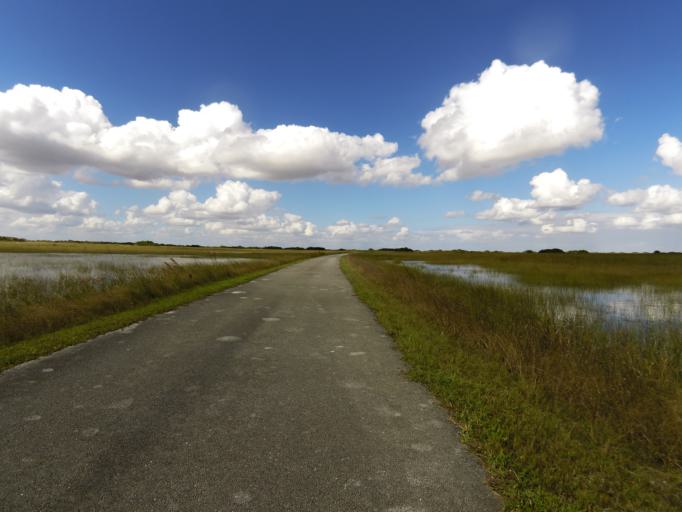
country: US
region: Florida
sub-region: Miami-Dade County
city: The Hammocks
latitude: 25.6780
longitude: -80.7631
